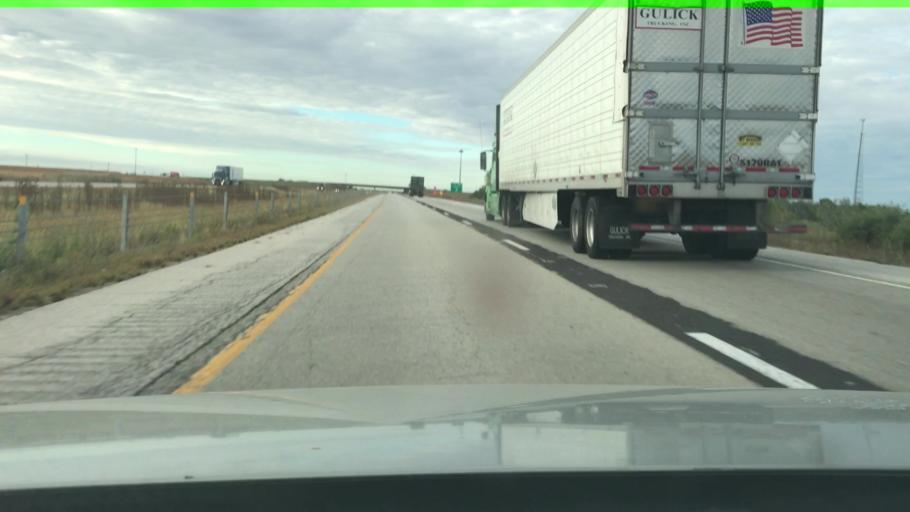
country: US
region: Illinois
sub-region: Livingston County
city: Odell
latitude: 41.0131
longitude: -88.5346
